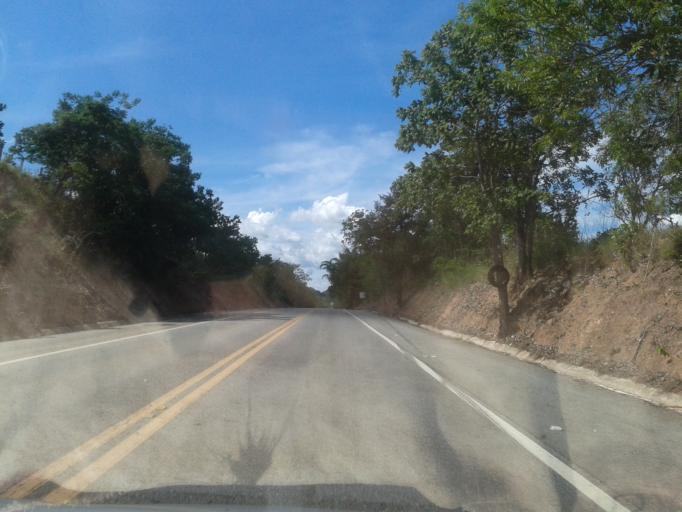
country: BR
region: Goias
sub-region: Goias
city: Goias
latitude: -15.7001
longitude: -50.1967
